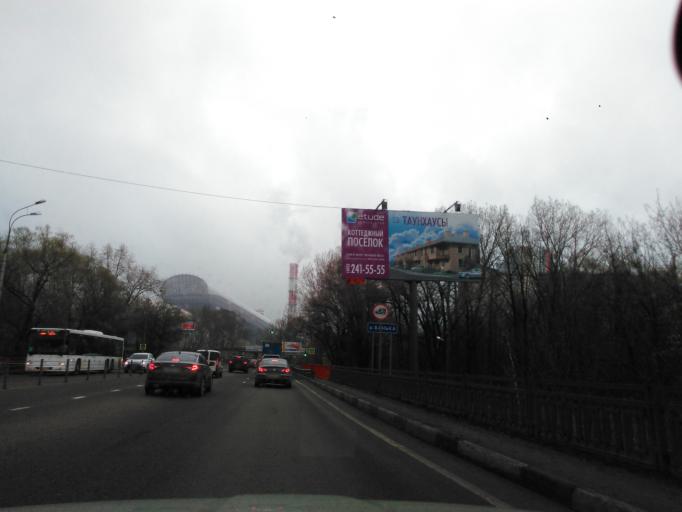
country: RU
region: Moskovskaya
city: Pavshino
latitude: 55.8180
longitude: 37.3497
